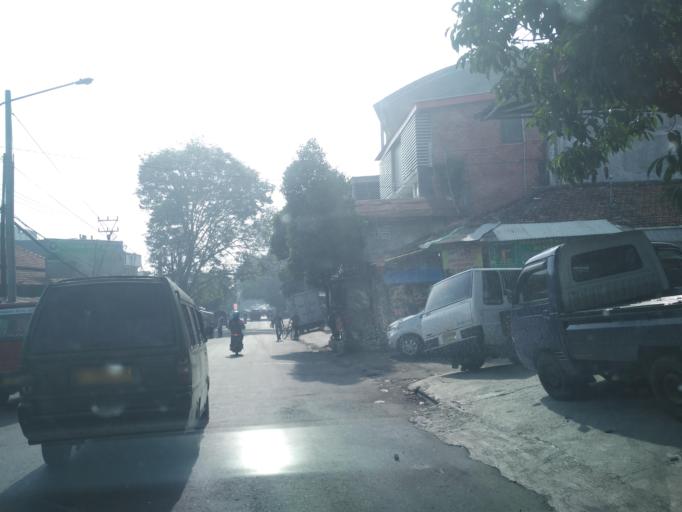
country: ID
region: West Java
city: Ciranjang-hilir
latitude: -6.8103
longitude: 107.1471
